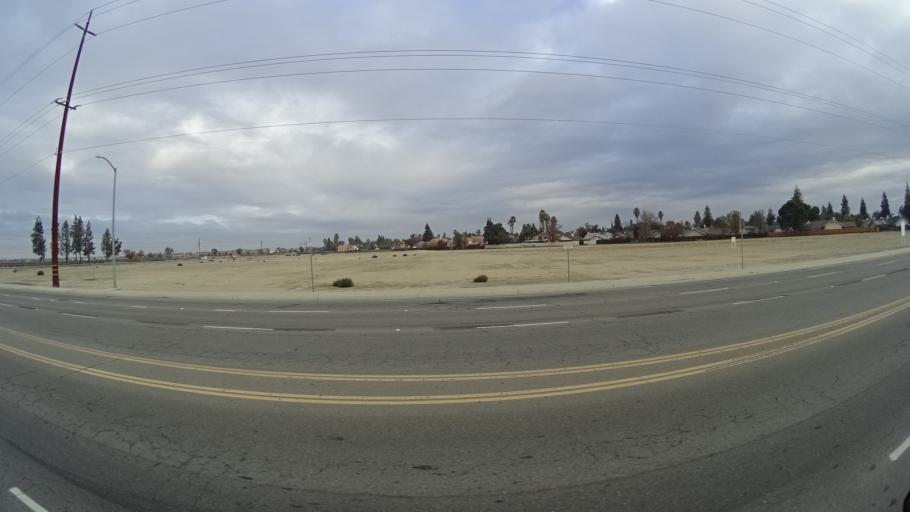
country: US
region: California
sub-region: Kern County
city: Greenacres
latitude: 35.2960
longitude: -119.0904
